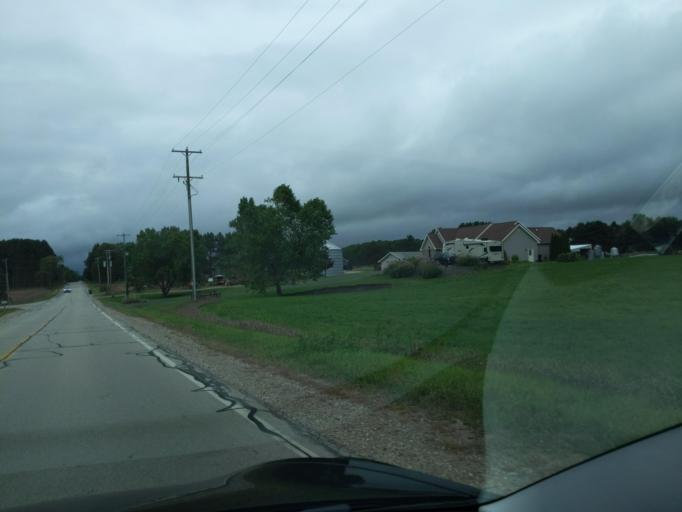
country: US
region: Michigan
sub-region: Grand Traverse County
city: Kingsley
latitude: 44.5900
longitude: -85.3529
